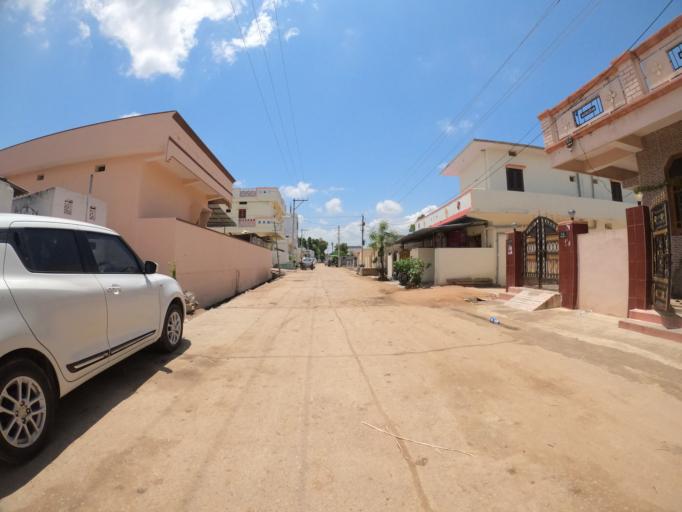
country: IN
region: Telangana
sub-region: Rangareddi
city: Singapur
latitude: 17.4405
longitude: 78.1581
